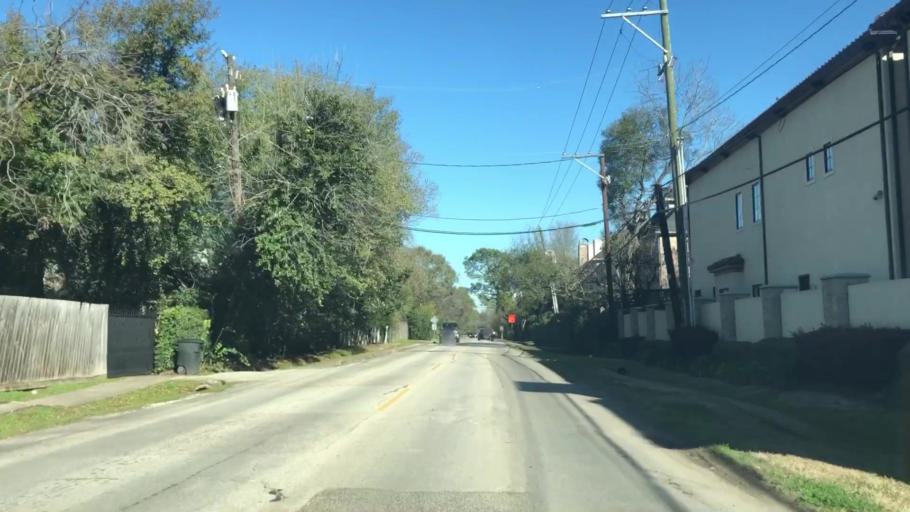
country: US
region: Texas
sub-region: Harris County
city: Hunters Creek Village
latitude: 29.7556
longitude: -95.4675
